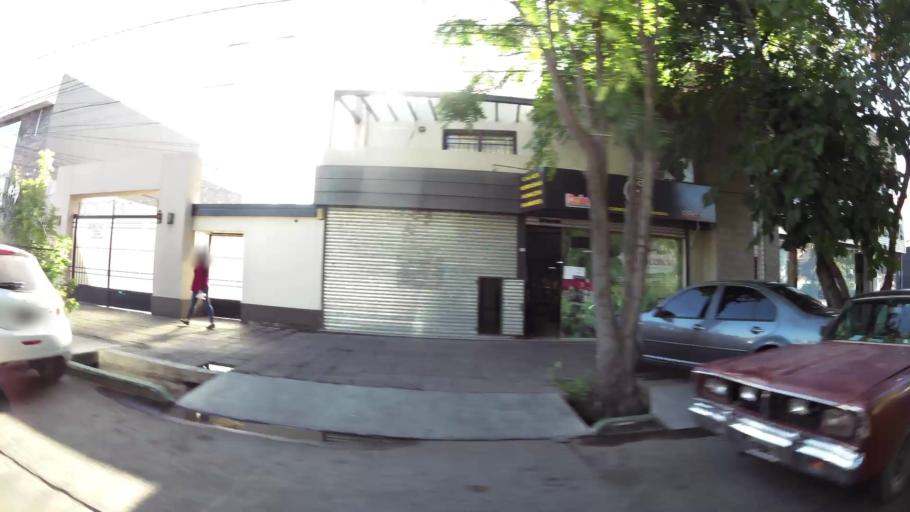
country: AR
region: Mendoza
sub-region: Departamento de Godoy Cruz
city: Godoy Cruz
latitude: -32.9230
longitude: -68.8499
